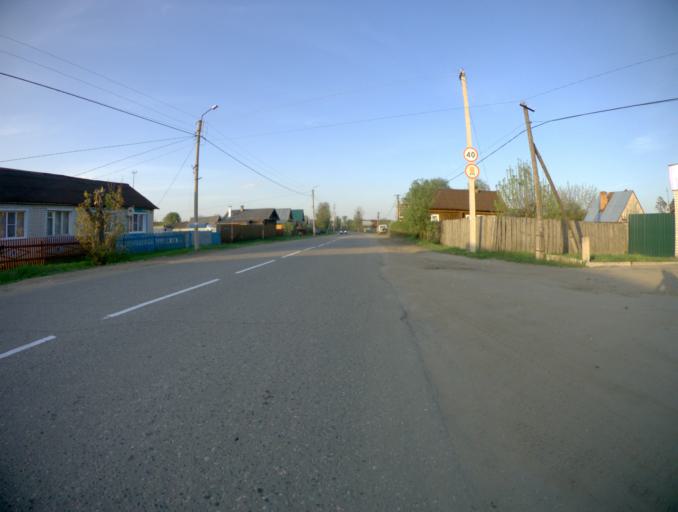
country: RU
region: Ivanovo
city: Yuzha
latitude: 56.5796
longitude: 41.9884
